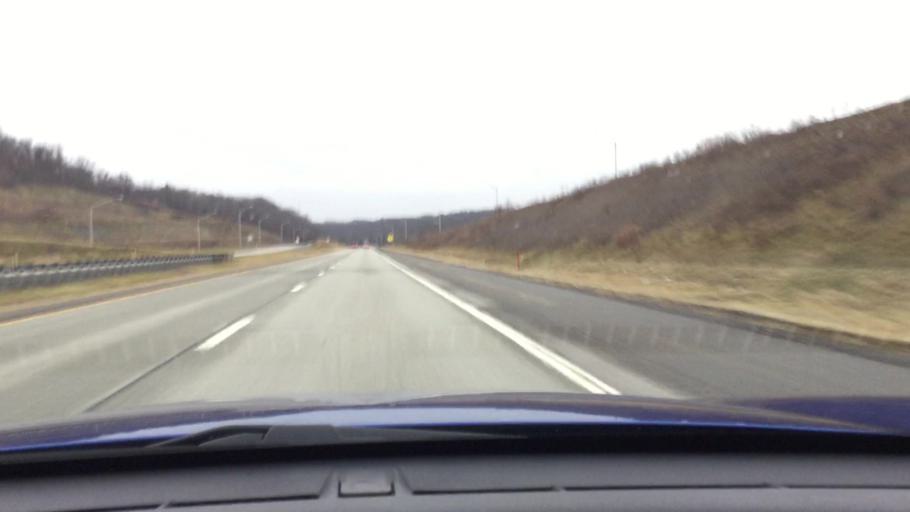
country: US
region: Pennsylvania
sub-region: Allegheny County
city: Imperial
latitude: 40.4241
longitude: -80.3200
